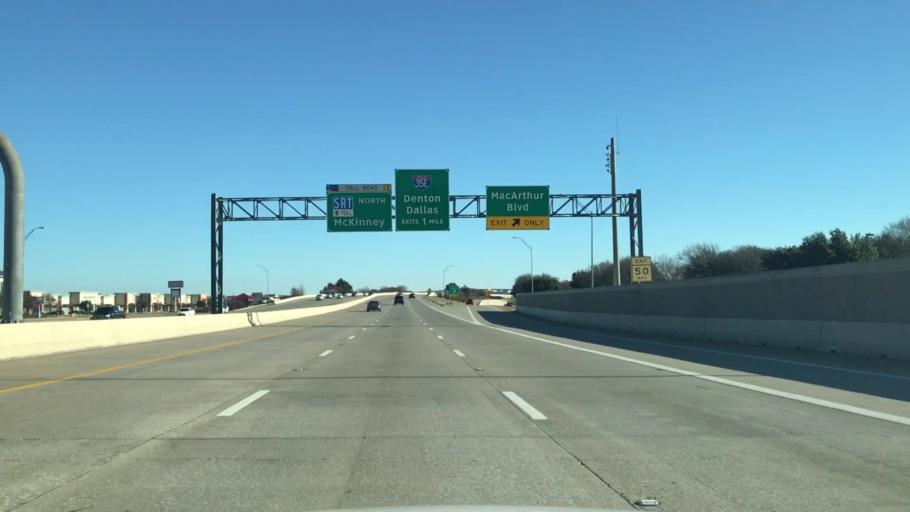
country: US
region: Texas
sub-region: Dallas County
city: Coppell
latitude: 32.9895
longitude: -96.9803
